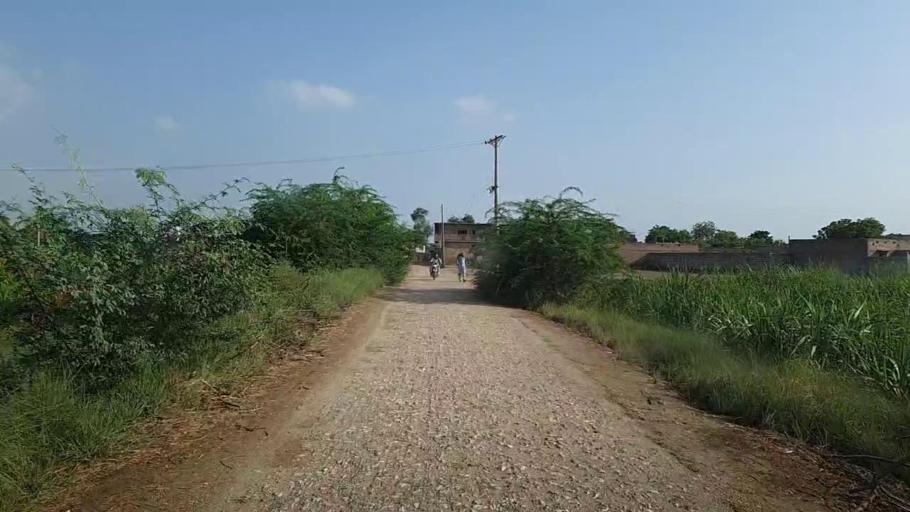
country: PK
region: Sindh
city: Bhiria
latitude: 26.8422
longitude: 68.2396
